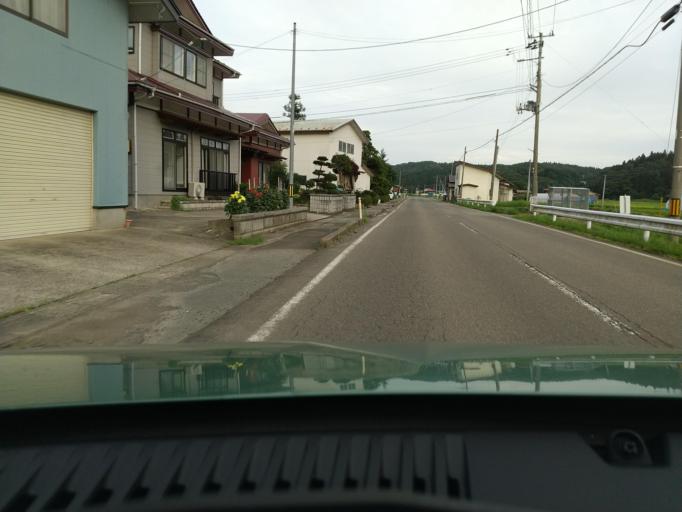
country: JP
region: Akita
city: Akita
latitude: 39.7828
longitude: 140.1273
